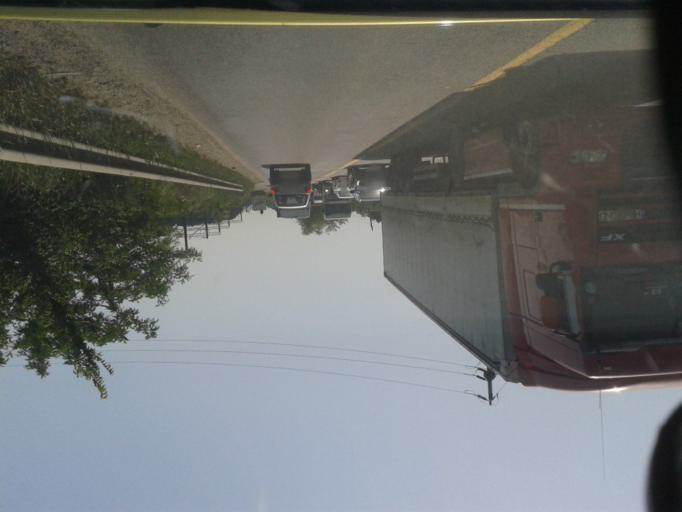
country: RO
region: Ilfov
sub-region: Voluntari City
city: Voluntari
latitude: 44.4924
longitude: 26.2114
